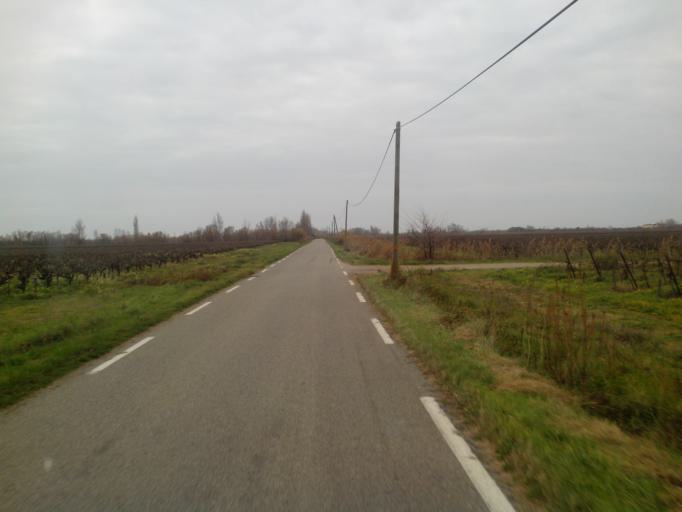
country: FR
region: Languedoc-Roussillon
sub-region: Departement du Gard
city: Vauvert
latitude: 43.5718
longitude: 4.3296
